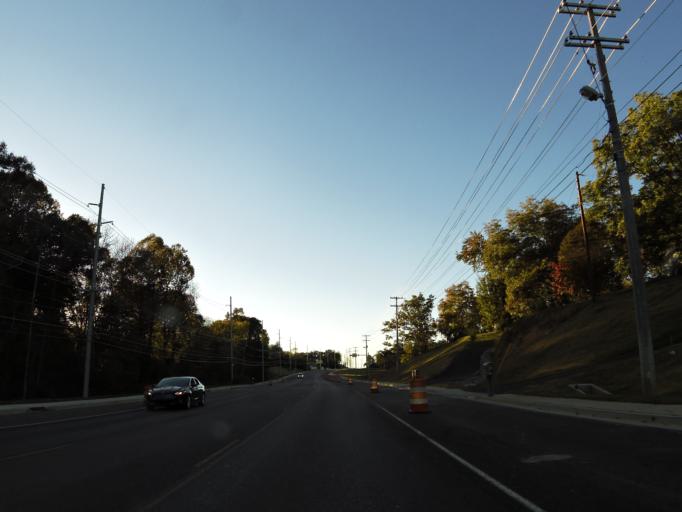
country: US
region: Tennessee
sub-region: Knox County
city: Knoxville
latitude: 35.9839
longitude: -84.0268
